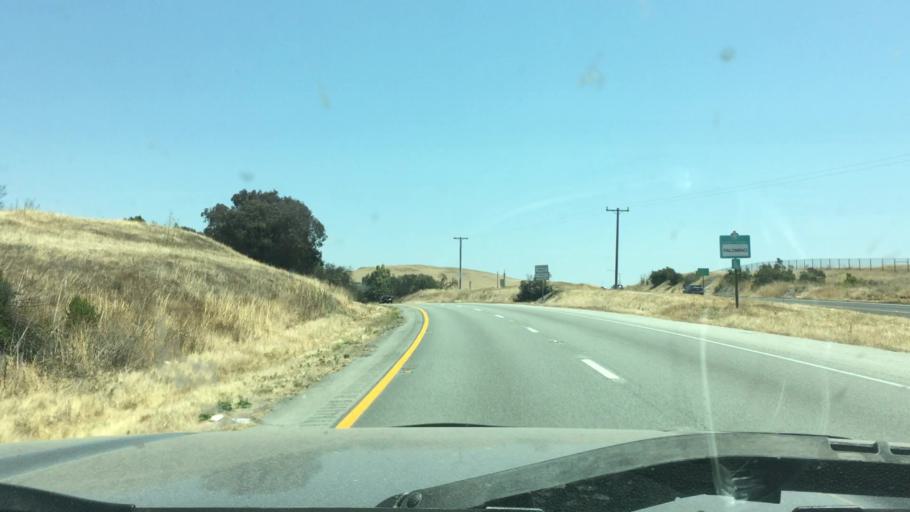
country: US
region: California
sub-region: San Benito County
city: San Juan Bautista
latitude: 36.9104
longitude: -121.5449
